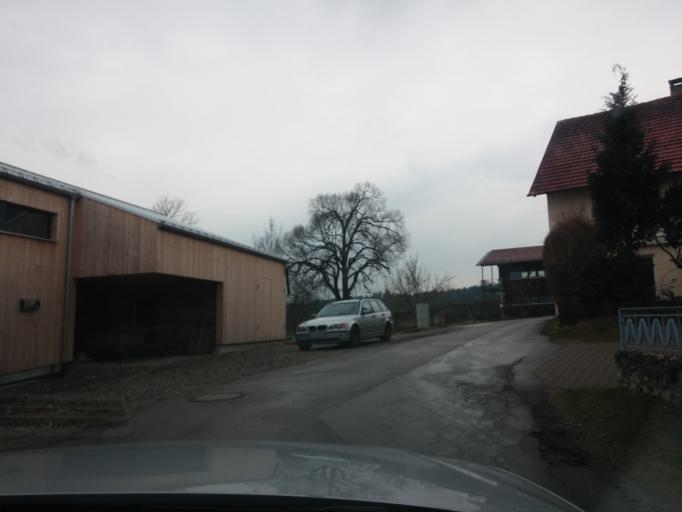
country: DE
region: Baden-Wuerttemberg
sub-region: Tuebingen Region
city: Leutkirch im Allgau
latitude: 47.8379
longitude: 10.0563
